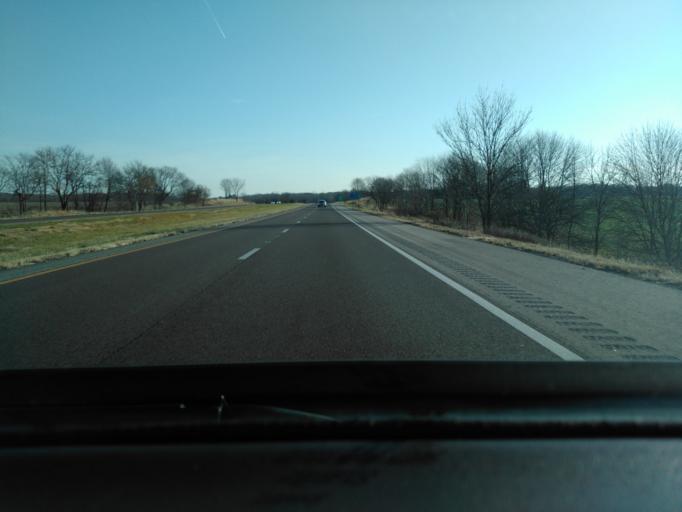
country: US
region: Illinois
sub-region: Madison County
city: Saint Jacob
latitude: 38.7652
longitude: -89.7675
